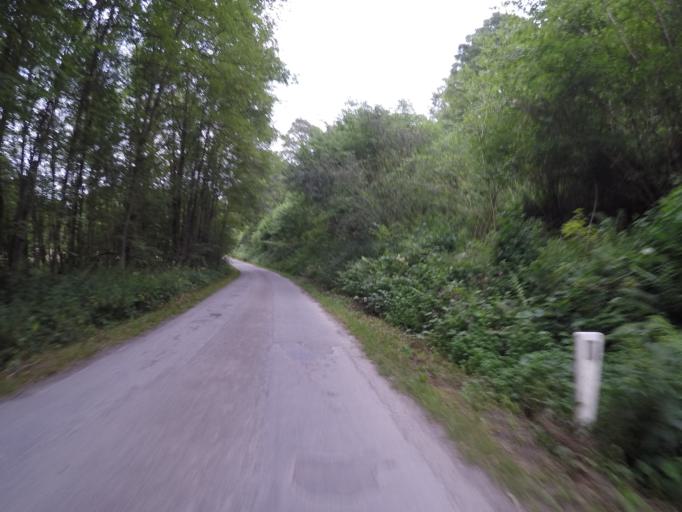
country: BE
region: Wallonia
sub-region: Province de Namur
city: Assesse
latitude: 50.3285
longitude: 4.9994
